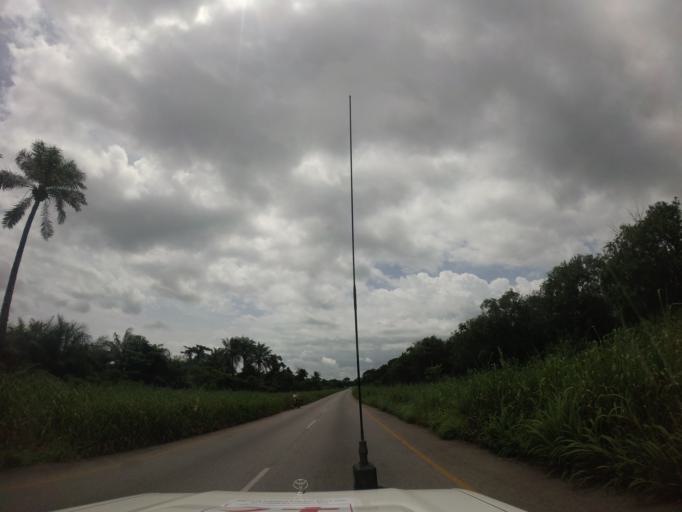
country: SL
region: Southern Province
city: Rotifunk
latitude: 8.4660
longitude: -12.6564
